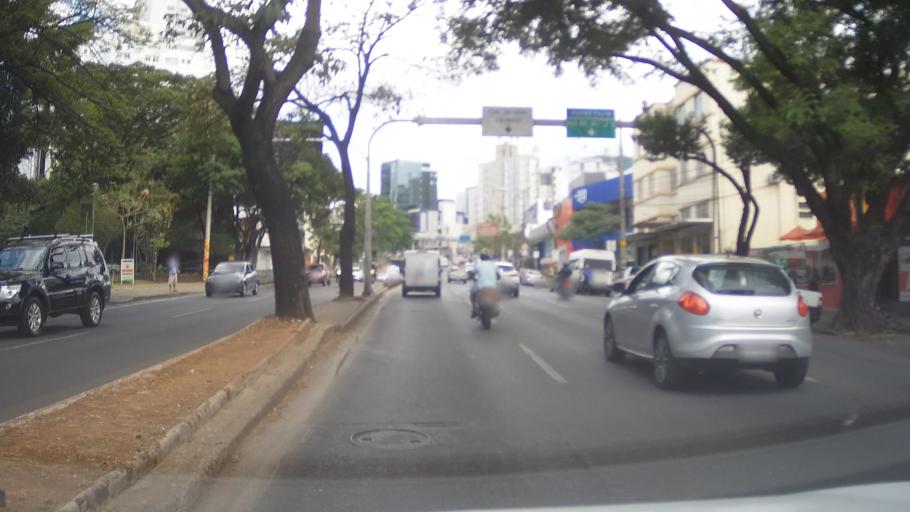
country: BR
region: Minas Gerais
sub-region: Belo Horizonte
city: Belo Horizonte
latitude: -19.9321
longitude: -43.9552
